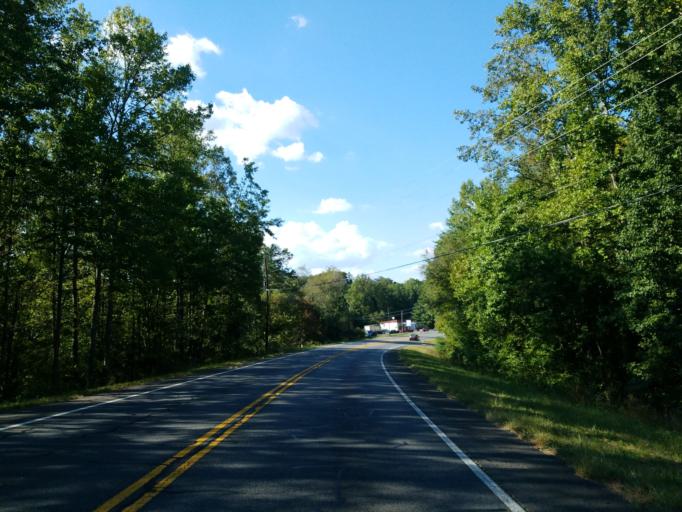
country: US
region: Georgia
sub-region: Bartow County
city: Rydal
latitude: 34.3473
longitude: -84.7230
